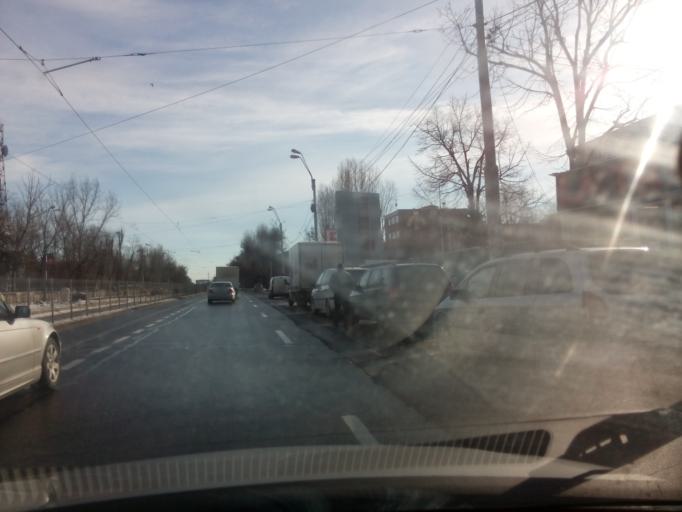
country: RO
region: Ilfov
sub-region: Comuna Popesti-Leordeni
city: Popesti-Leordeni
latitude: 44.3856
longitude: 26.1402
